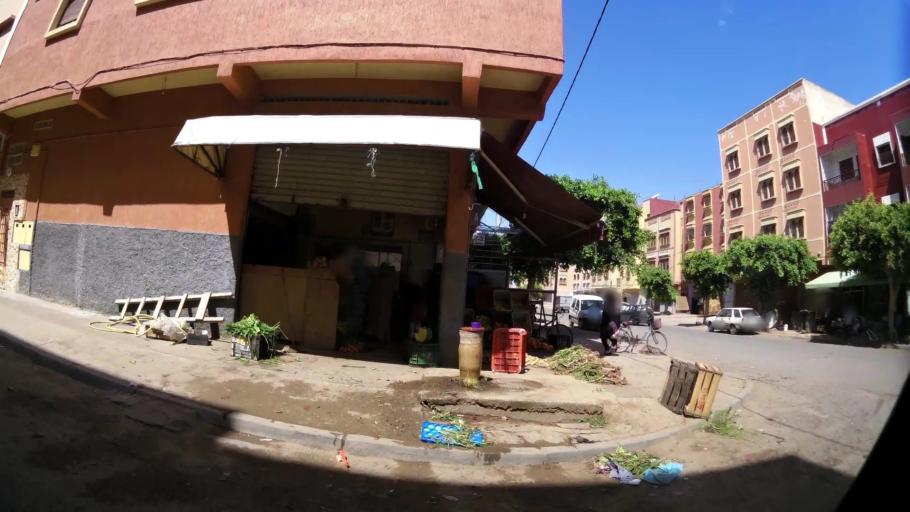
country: MA
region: Souss-Massa-Draa
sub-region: Inezgane-Ait Mellou
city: Inezgane
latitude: 30.3344
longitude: -9.5054
